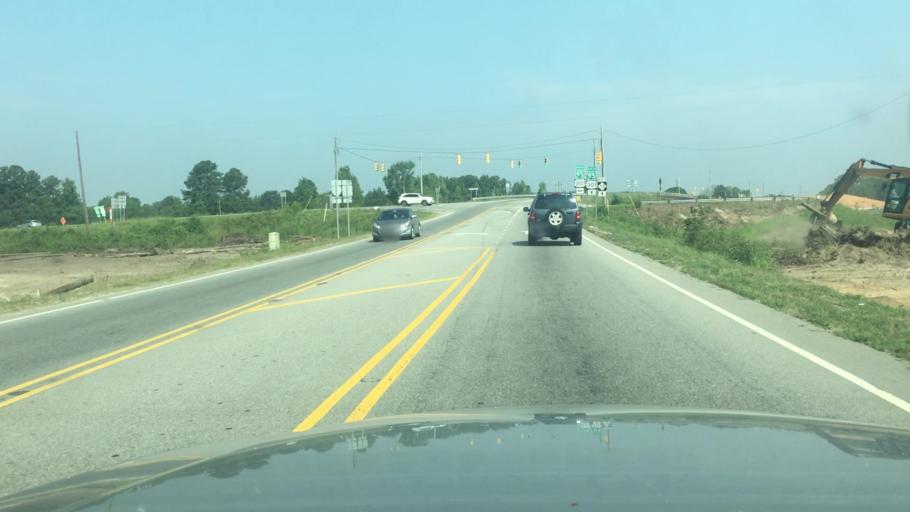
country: US
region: North Carolina
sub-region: Cumberland County
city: Hope Mills
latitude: 34.9433
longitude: -78.9290
